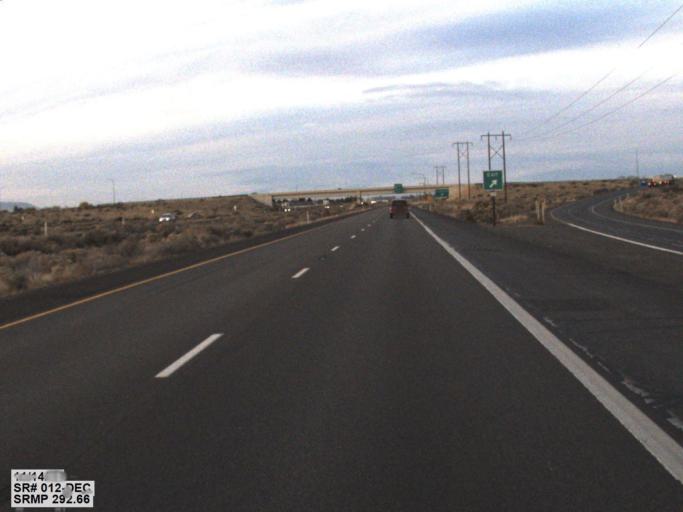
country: US
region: Washington
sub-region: Franklin County
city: Pasco
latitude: 46.2367
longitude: -119.0526
